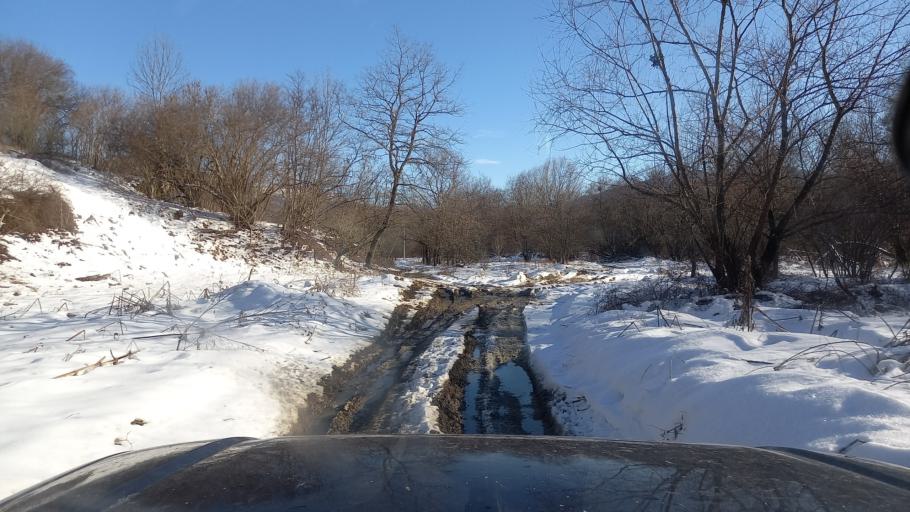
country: RU
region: Adygeya
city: Kamennomostskiy
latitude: 44.2051
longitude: 40.1507
